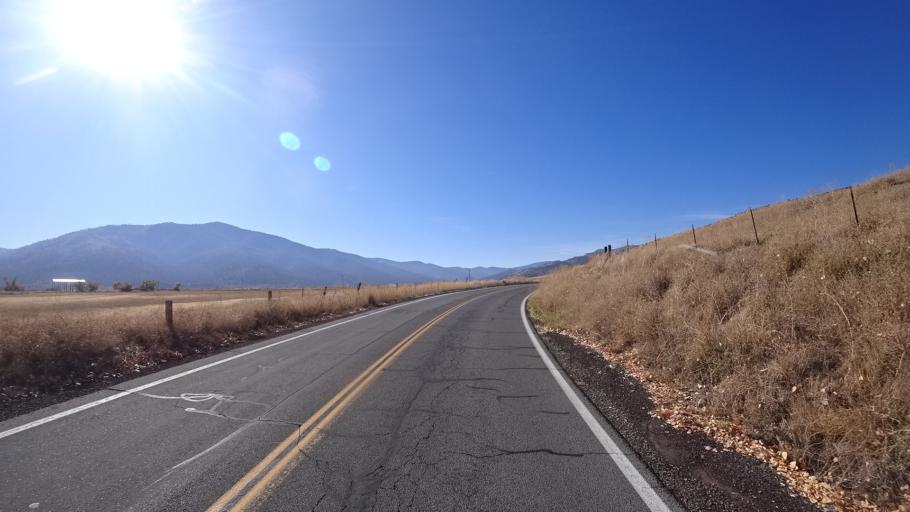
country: US
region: California
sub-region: Siskiyou County
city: Weed
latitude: 41.5114
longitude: -122.5260
